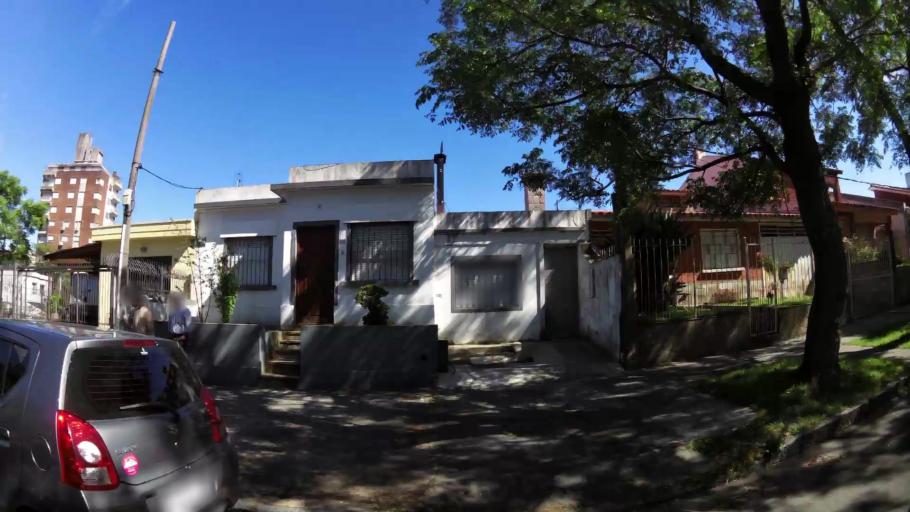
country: UY
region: Montevideo
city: Montevideo
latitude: -34.8888
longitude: -56.1427
